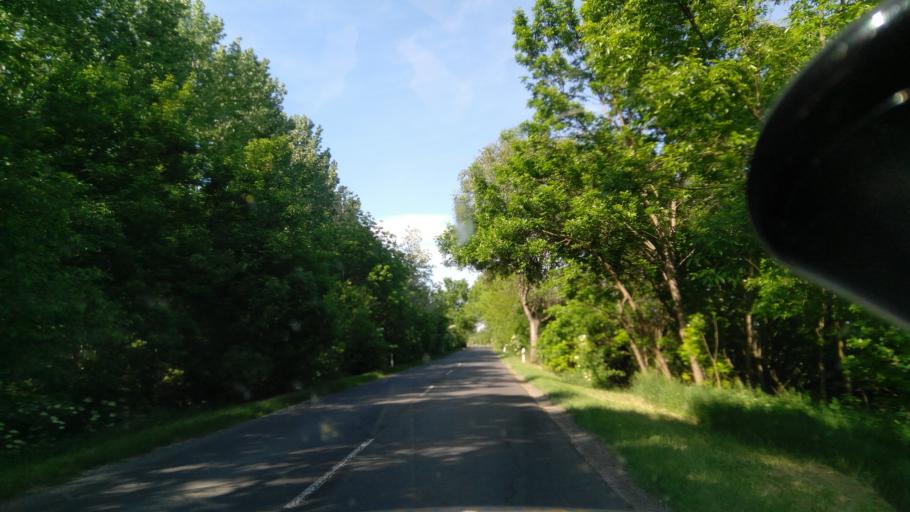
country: HU
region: Bekes
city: Gyula
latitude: 46.6779
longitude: 21.3024
